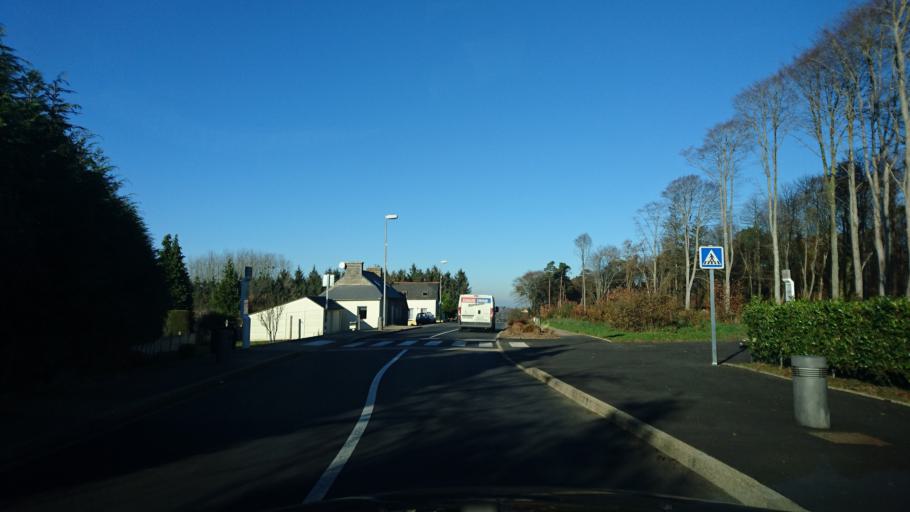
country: FR
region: Brittany
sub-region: Departement des Cotes-d'Armor
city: Pledran
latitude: 48.4507
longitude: -2.7521
